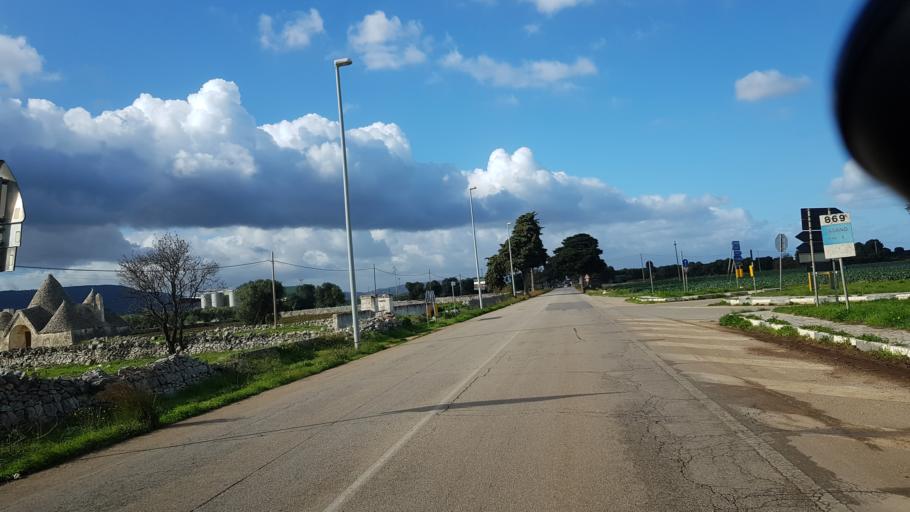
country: IT
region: Apulia
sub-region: Provincia di Brindisi
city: Montalbano
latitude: 40.7865
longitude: 17.4713
